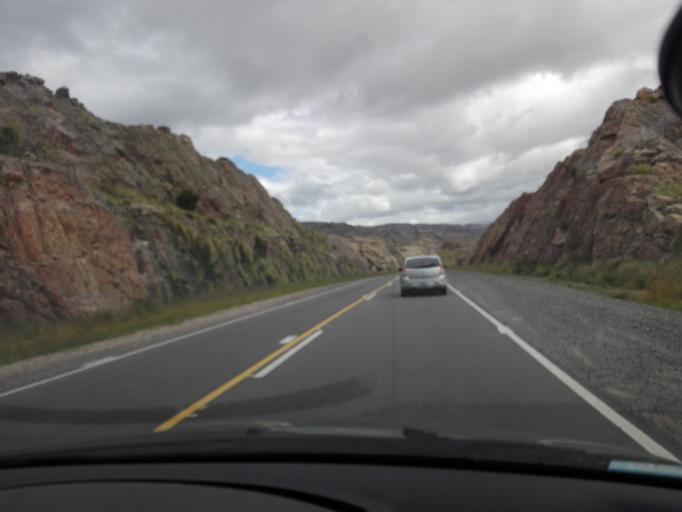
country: AR
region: Cordoba
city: Mina Clavero
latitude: -31.6404
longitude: -64.9061
